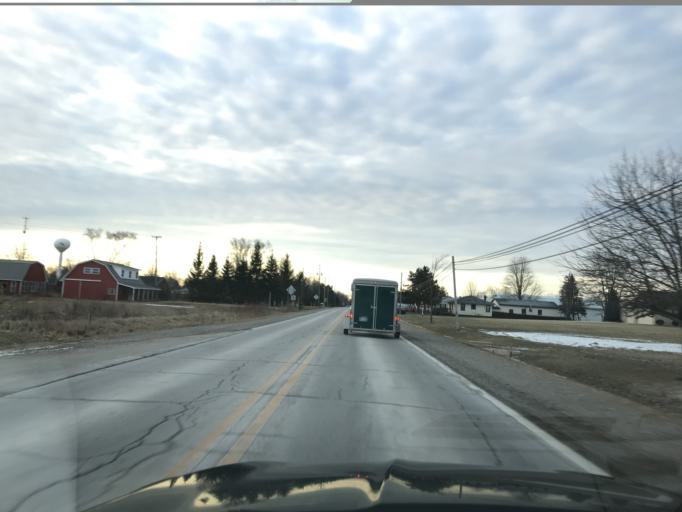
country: US
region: Michigan
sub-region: Macomb County
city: Armada
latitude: 42.8550
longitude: -82.8850
